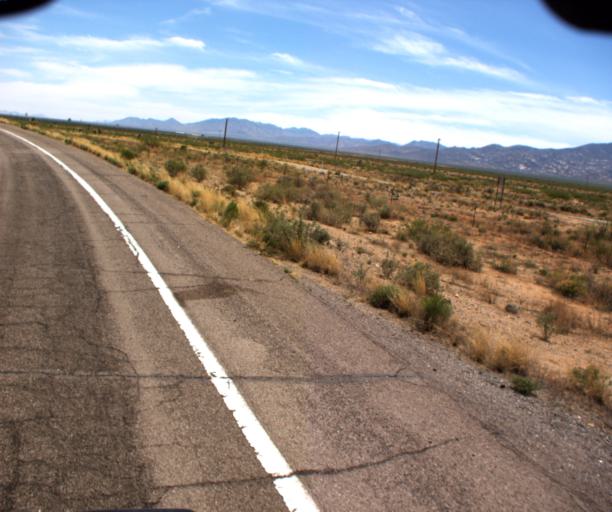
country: US
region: Arizona
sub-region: Cochise County
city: Willcox
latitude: 32.3292
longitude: -109.5156
